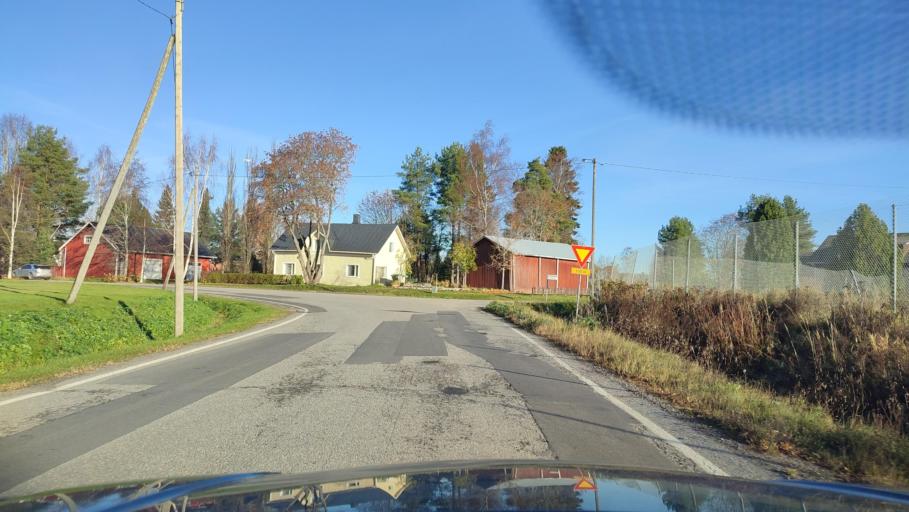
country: FI
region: Southern Ostrobothnia
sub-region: Suupohja
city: Karijoki
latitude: 62.2319
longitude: 21.6541
